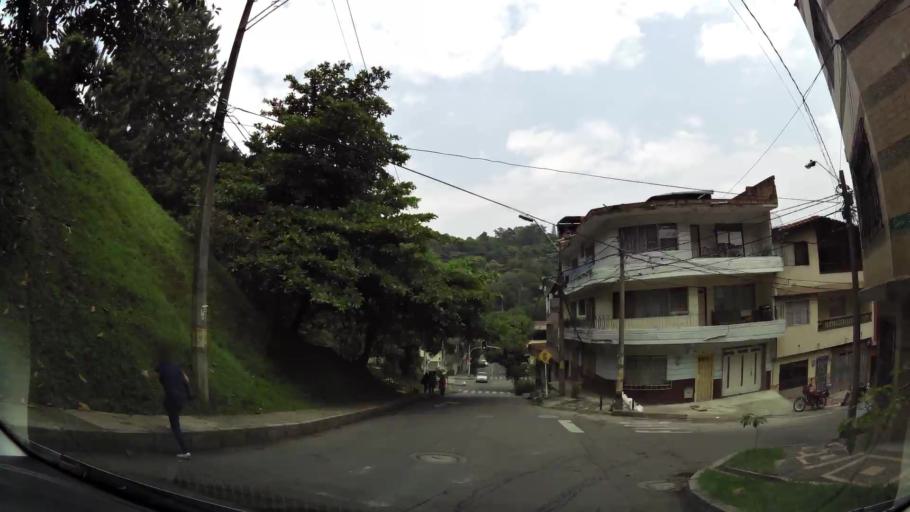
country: CO
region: Antioquia
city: Medellin
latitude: 6.2348
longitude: -75.5628
